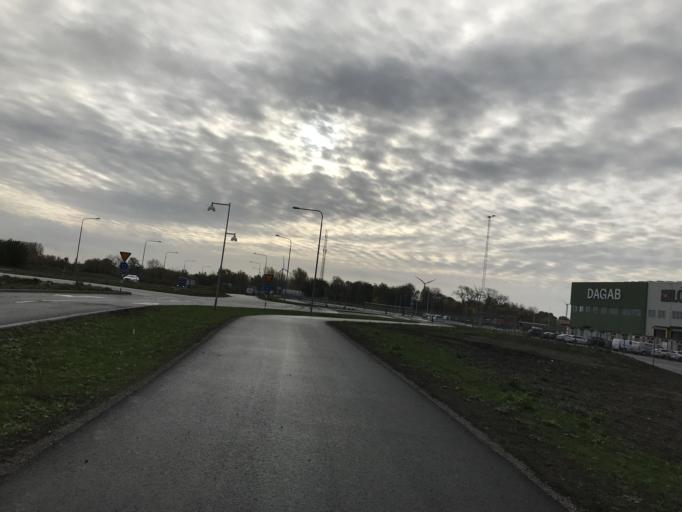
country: SE
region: Skane
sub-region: Landskrona
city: Landskrona
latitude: 55.8771
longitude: 12.8659
